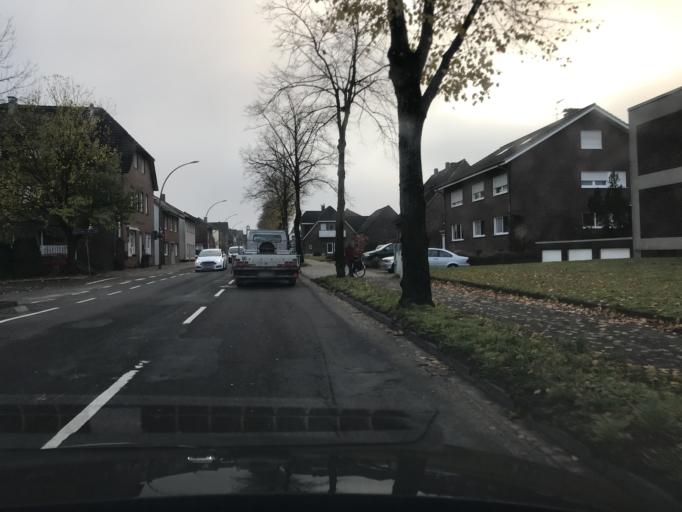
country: DE
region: North Rhine-Westphalia
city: Oelde
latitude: 51.8157
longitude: 8.1383
